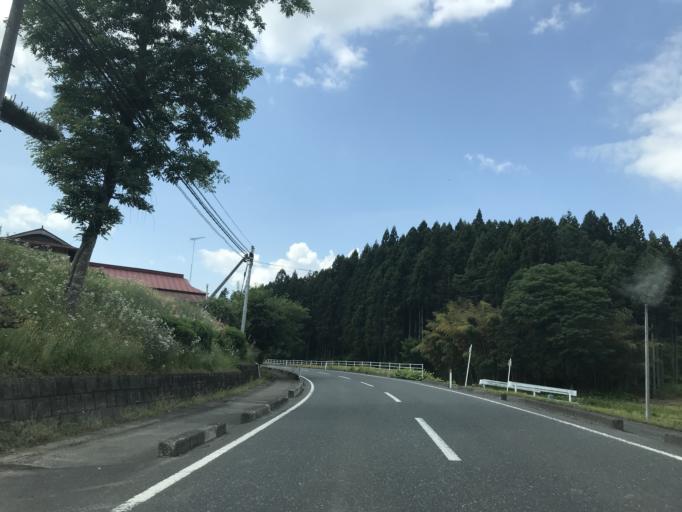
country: JP
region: Miyagi
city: Furukawa
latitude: 38.7527
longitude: 140.9545
